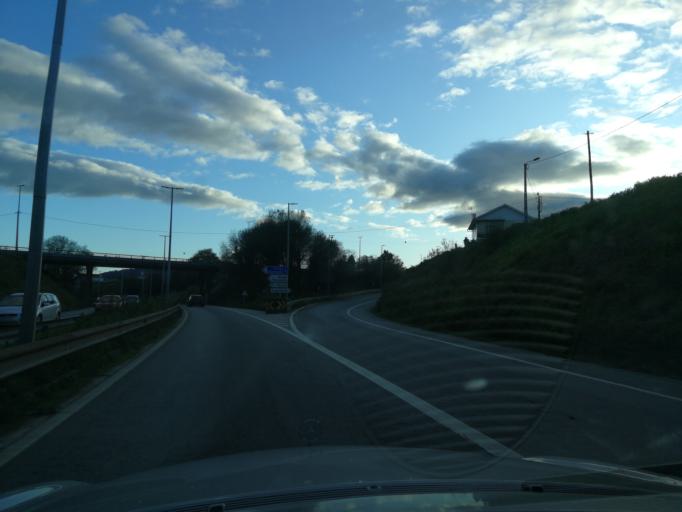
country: PT
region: Braga
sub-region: Barcelos
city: Vila Frescainha
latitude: 41.5325
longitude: -8.6400
